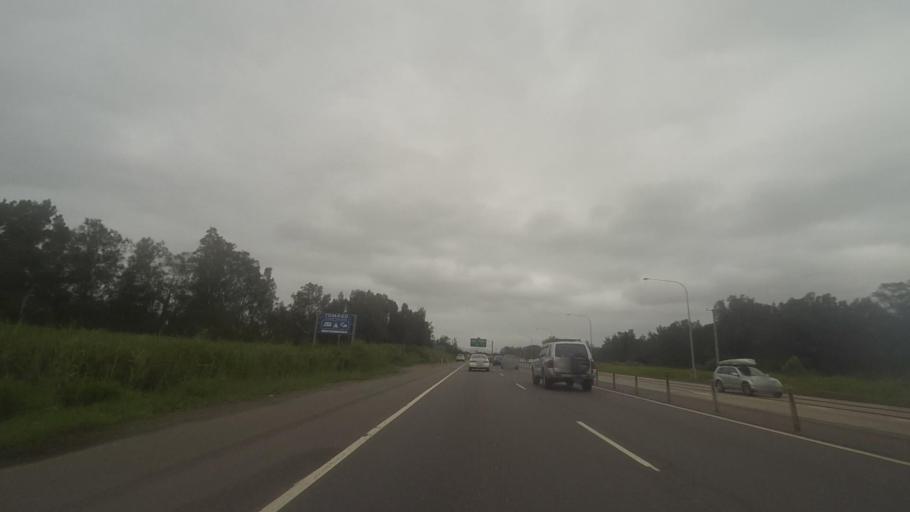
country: AU
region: New South Wales
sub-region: Newcastle
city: Beresfield
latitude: -32.8169
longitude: 151.6958
